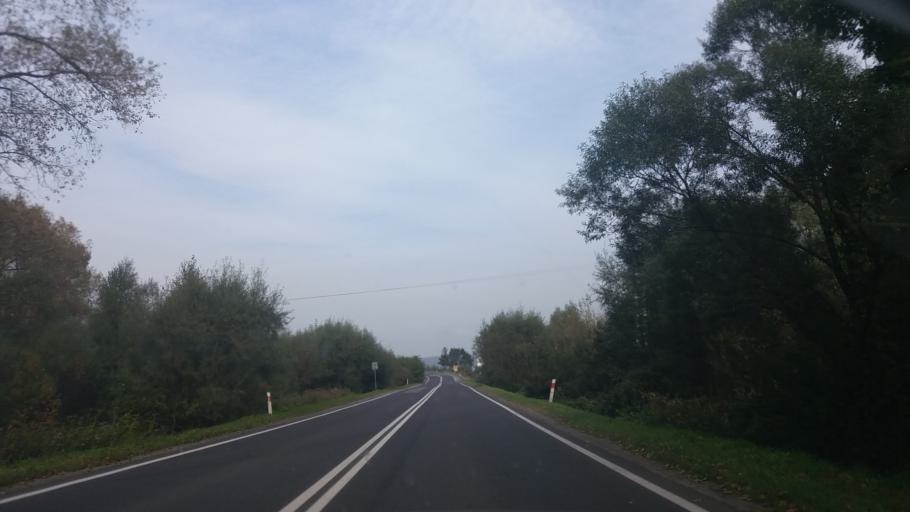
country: PL
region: Lesser Poland Voivodeship
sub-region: Powiat oswiecimski
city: Zator
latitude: 50.0245
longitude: 19.4357
